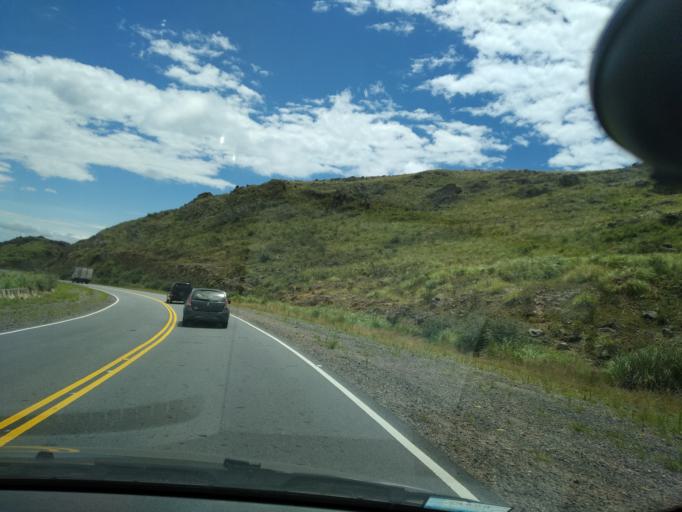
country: AR
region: Cordoba
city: Cuesta Blanca
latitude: -31.6047
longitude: -64.6995
